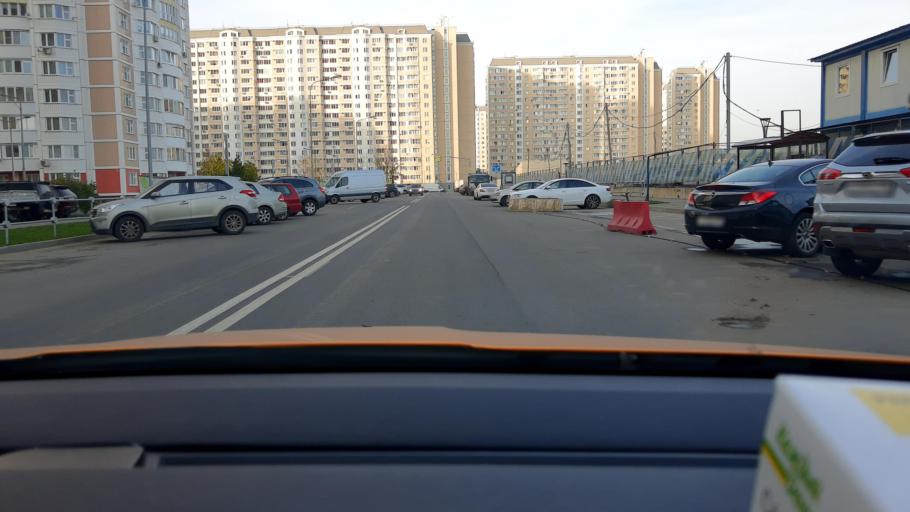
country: RU
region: Moskovskaya
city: Moskovskiy
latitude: 55.6006
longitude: 37.3671
